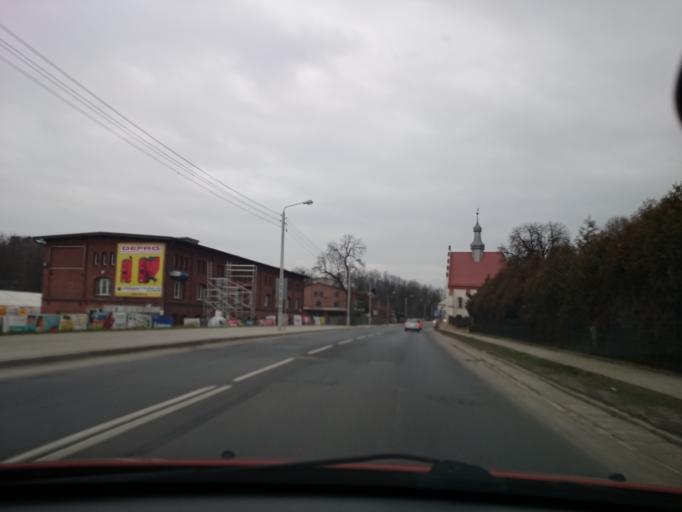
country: PL
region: Opole Voivodeship
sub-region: Powiat nyski
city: Nysa
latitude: 50.4797
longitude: 17.3179
